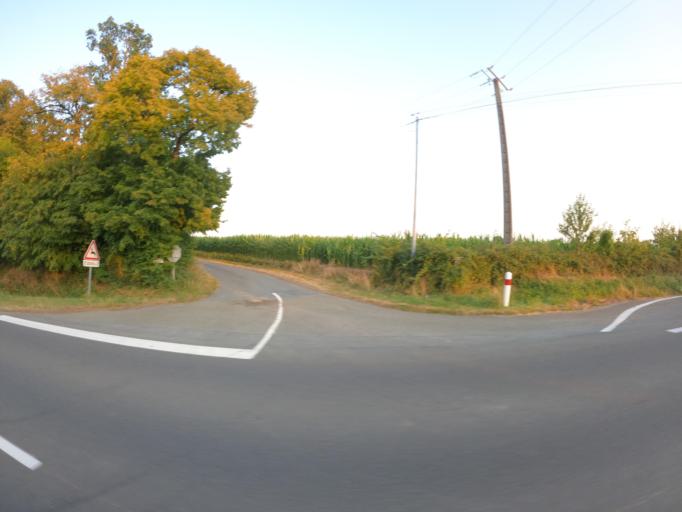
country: FR
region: Pays de la Loire
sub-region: Departement de la Mayenne
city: Meslay-du-Maine
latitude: 47.8646
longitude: -0.5634
